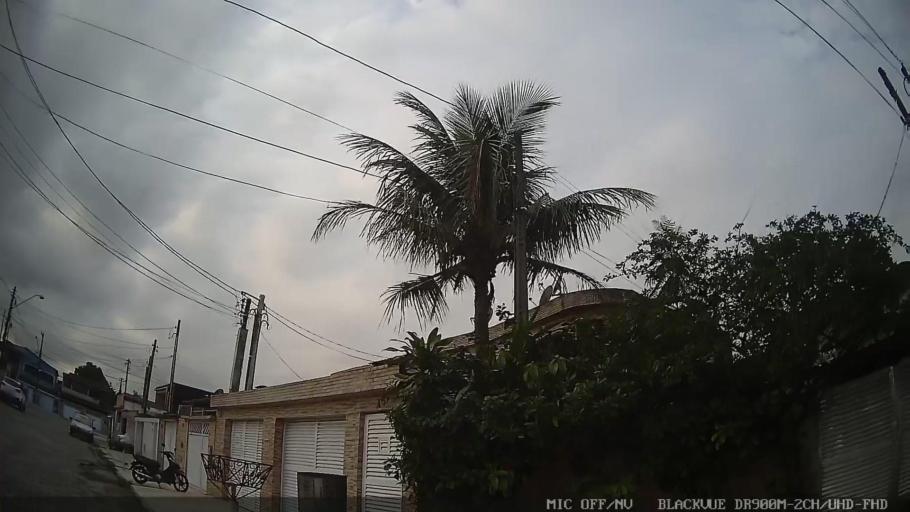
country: BR
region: Sao Paulo
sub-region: Guaruja
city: Guaruja
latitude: -23.9563
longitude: -46.2826
